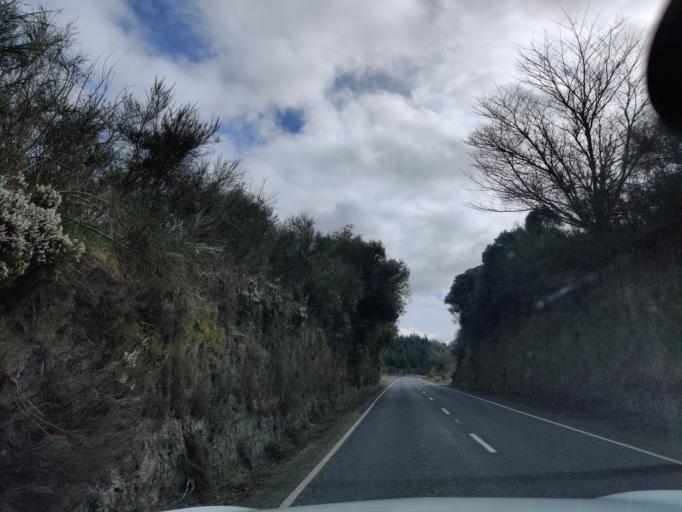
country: NZ
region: Waikato
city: Turangi
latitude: -38.7248
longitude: 175.6586
